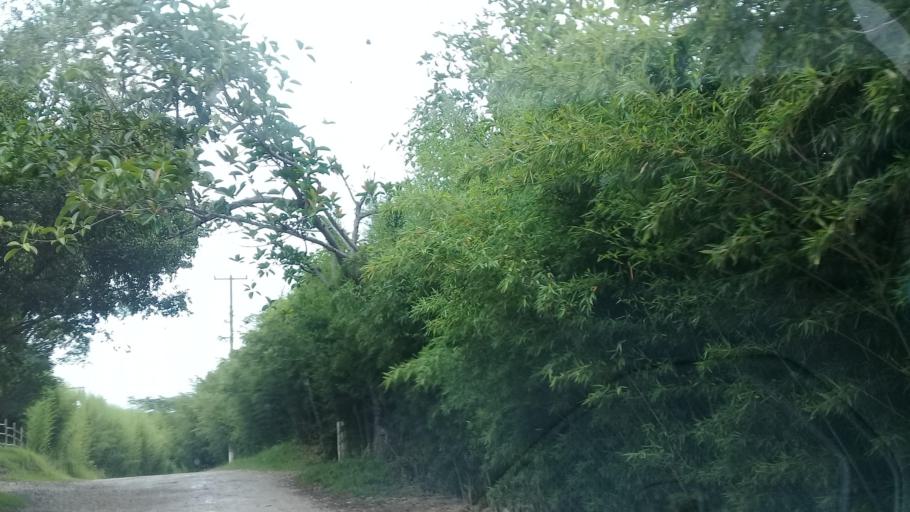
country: MX
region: Veracruz
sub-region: Emiliano Zapata
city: Jacarandas
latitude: 19.5048
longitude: -96.8498
